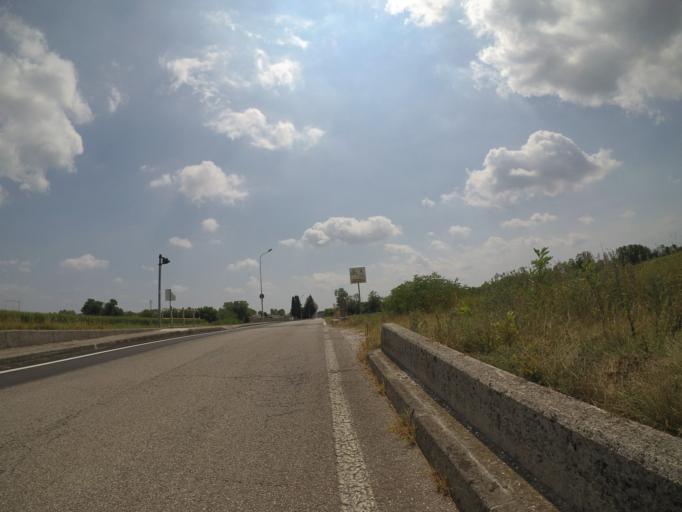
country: IT
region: Friuli Venezia Giulia
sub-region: Provincia di Udine
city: Basiliano
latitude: 46.0004
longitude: 13.0762
